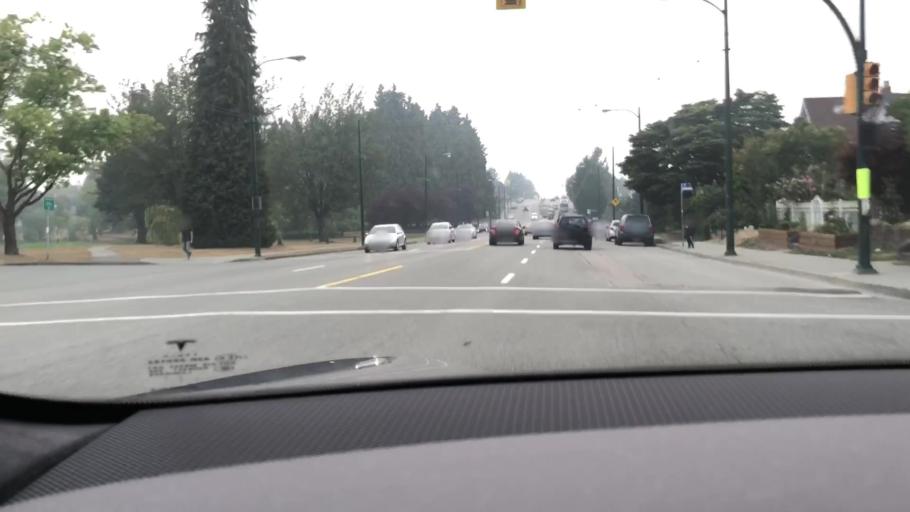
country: CA
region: British Columbia
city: Vancouver
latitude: 49.2328
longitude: -123.0848
